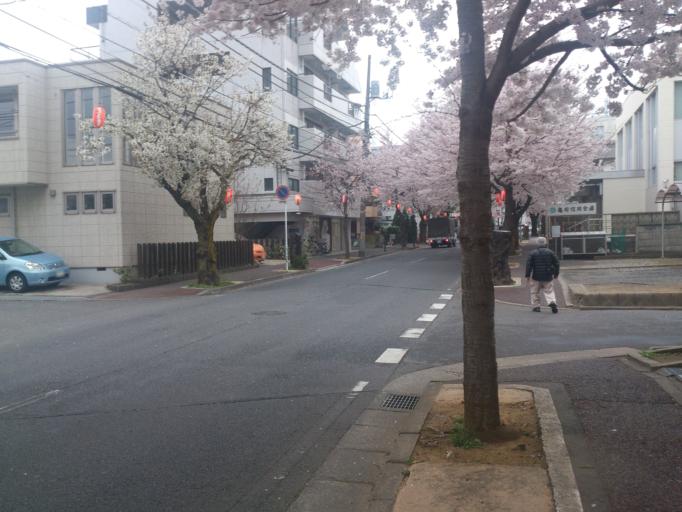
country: JP
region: Chiba
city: Matsudo
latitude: 35.7951
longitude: 139.9407
